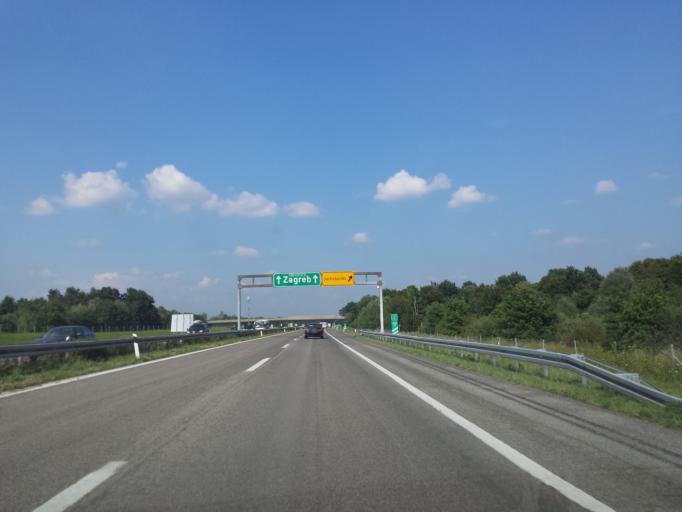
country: HR
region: Zagrebacka
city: Jastrebarsko
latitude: 45.6433
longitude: 15.6766
